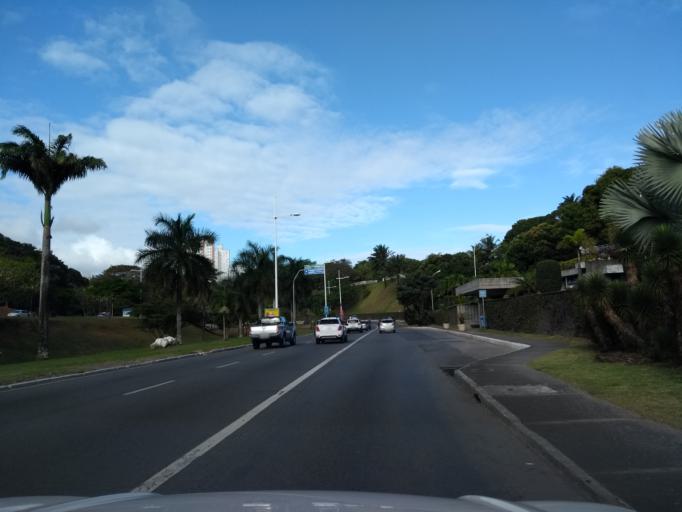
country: BR
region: Bahia
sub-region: Salvador
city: Salvador
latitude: -13.0003
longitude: -38.4815
